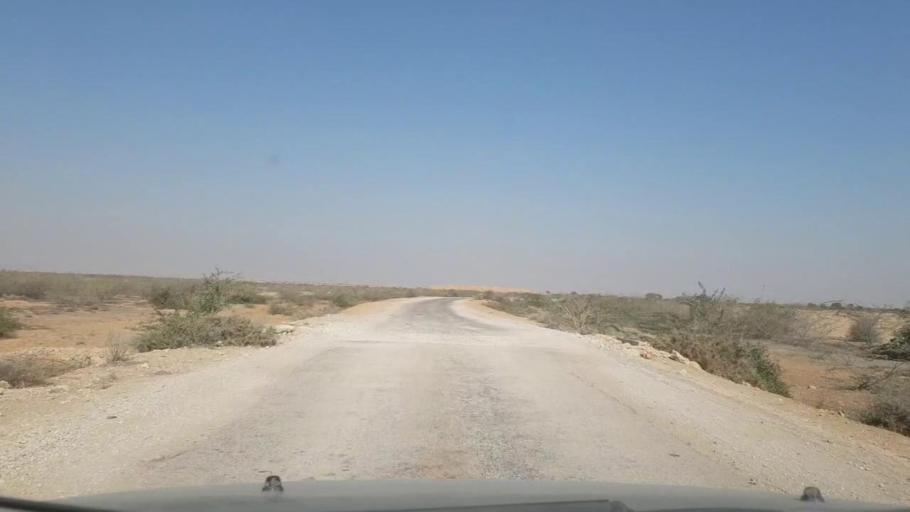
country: PK
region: Sindh
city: Thatta
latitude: 24.9507
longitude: 67.9532
